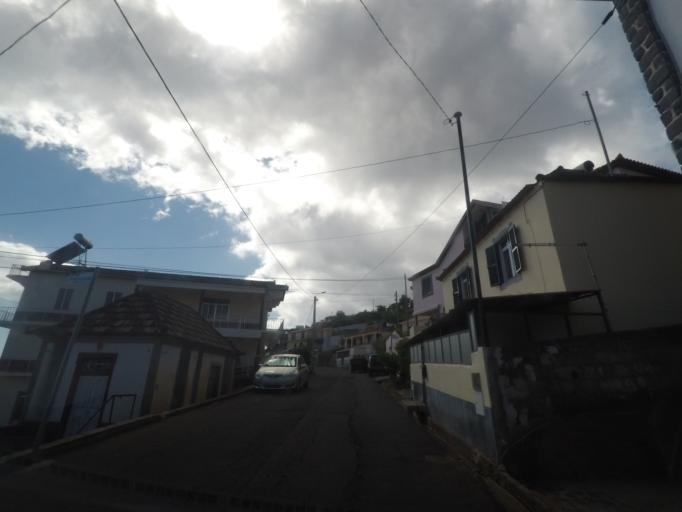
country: PT
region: Madeira
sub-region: Ribeira Brava
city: Campanario
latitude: 32.6736
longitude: -17.0507
